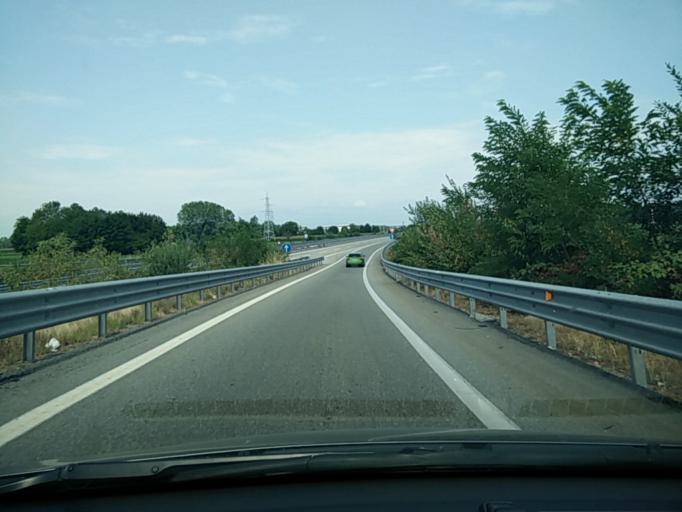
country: IT
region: Piedmont
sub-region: Provincia di Torino
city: Brandizzo
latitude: 45.1729
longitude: 7.8072
